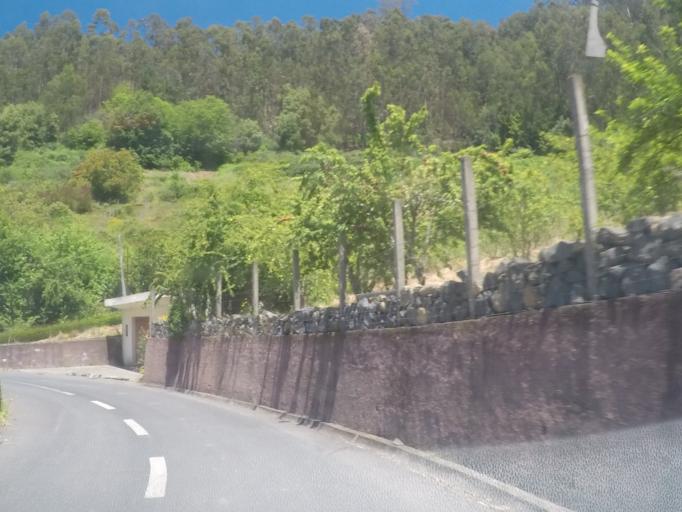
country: PT
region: Madeira
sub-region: Camara de Lobos
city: Curral das Freiras
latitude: 32.6898
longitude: -16.9744
